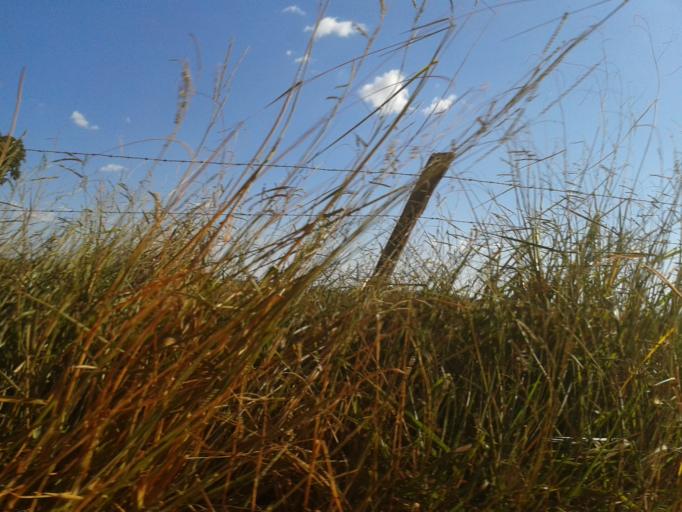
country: BR
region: Minas Gerais
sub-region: Centralina
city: Centralina
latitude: -18.7446
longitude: -49.1890
